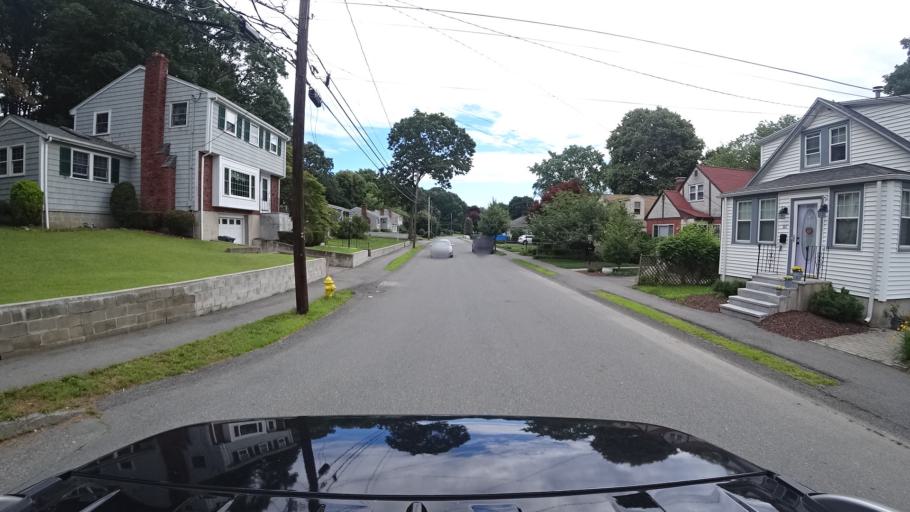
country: US
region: Massachusetts
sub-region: Norfolk County
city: Dedham
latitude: 42.2290
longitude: -71.1450
